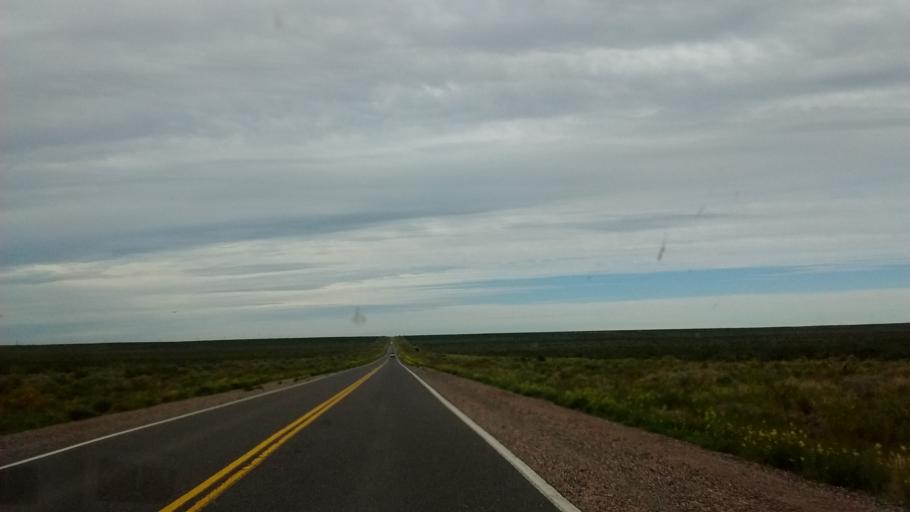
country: AR
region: Rio Negro
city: Catriel
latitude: -38.2340
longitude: -67.9830
